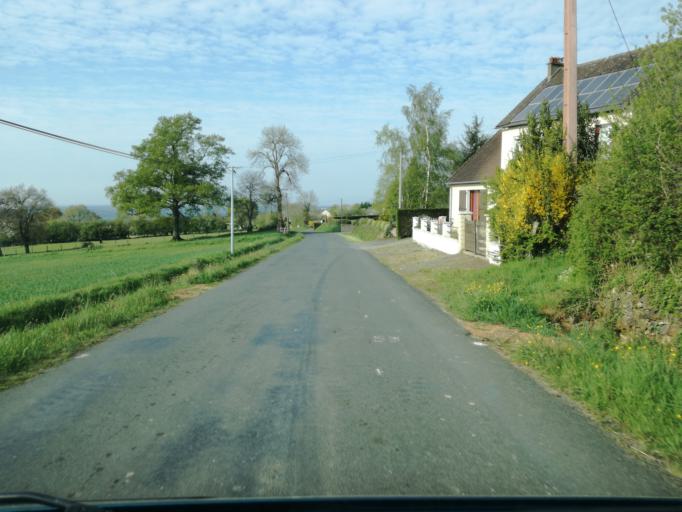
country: FR
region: Pays de la Loire
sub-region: Departement de la Sarthe
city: Brulon
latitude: 48.0354
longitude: -0.2671
